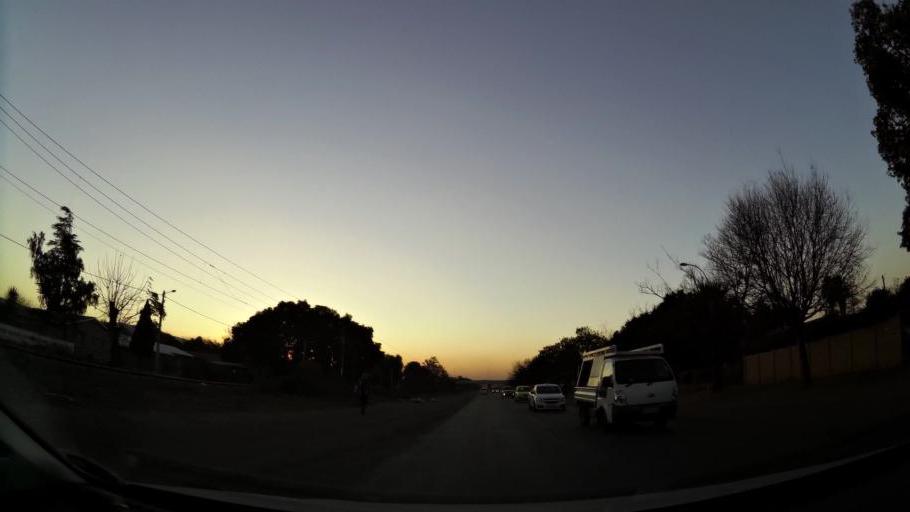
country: ZA
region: North-West
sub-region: Bojanala Platinum District Municipality
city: Rustenburg
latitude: -25.6581
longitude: 27.2460
